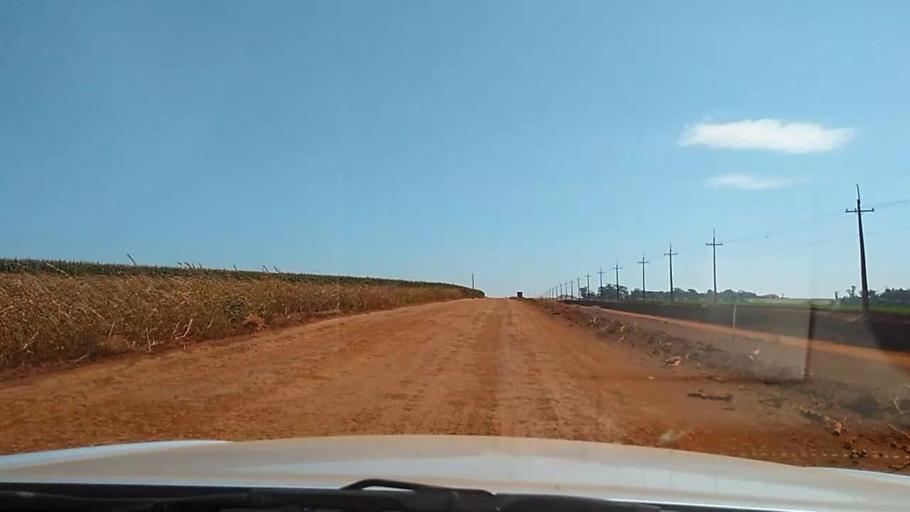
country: PY
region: Alto Parana
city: Naranjal
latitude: -25.9723
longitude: -55.2353
